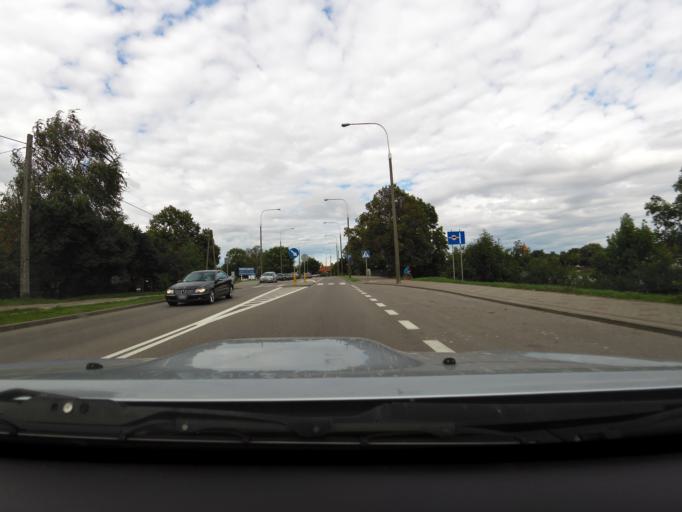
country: PL
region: Pomeranian Voivodeship
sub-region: Powiat malborski
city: Malbork
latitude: 54.0406
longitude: 19.0237
